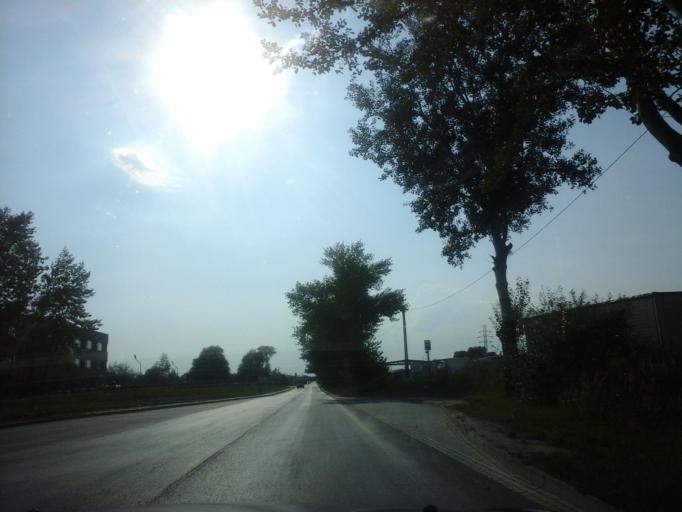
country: PL
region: Lesser Poland Voivodeship
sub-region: Powiat wielicki
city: Czarnochowice
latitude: 50.0330
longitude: 20.0514
